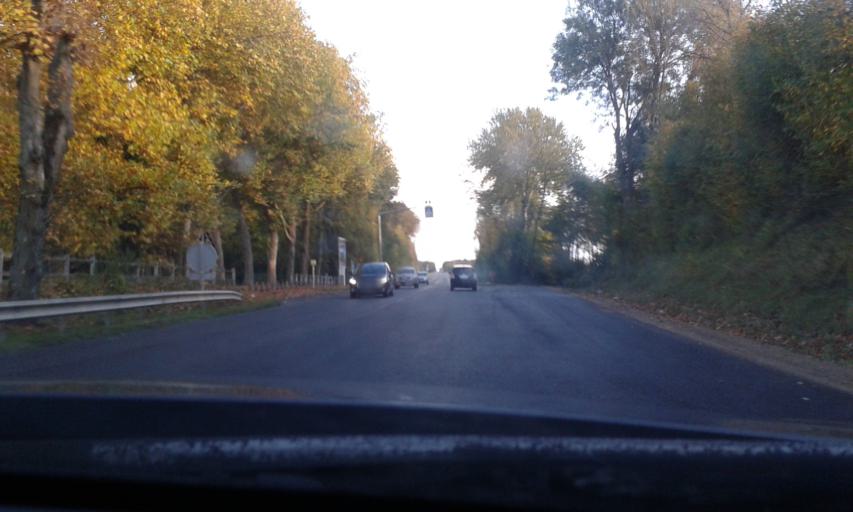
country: FR
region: Centre
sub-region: Departement d'Eure-et-Loir
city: Sours
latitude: 48.4036
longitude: 1.5503
